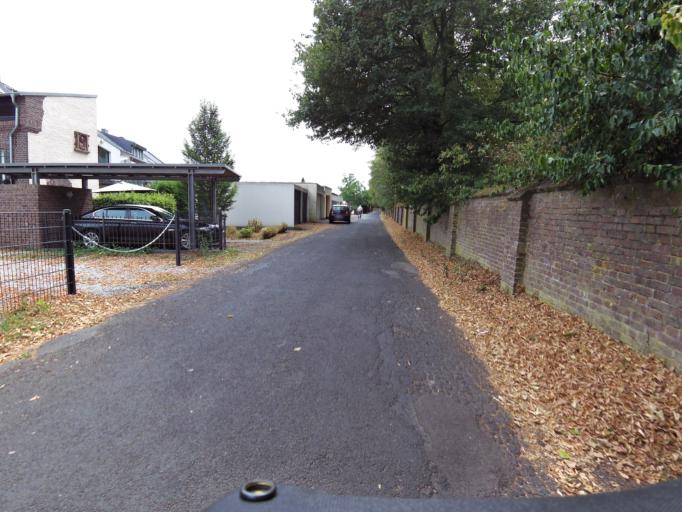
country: DE
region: North Rhine-Westphalia
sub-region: Regierungsbezirk Dusseldorf
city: Kevelaer
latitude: 51.5796
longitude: 6.2506
